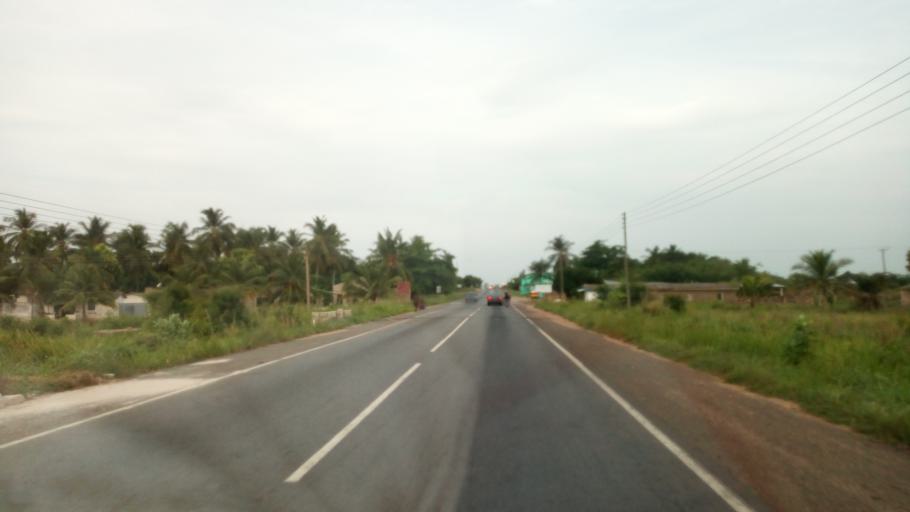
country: GH
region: Volta
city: Keta
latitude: 6.0671
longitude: 1.0157
